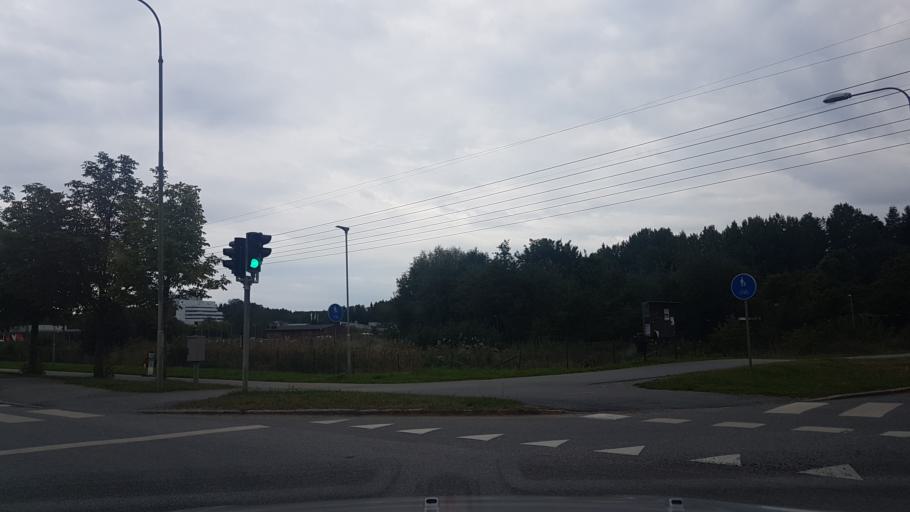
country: SE
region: Stockholm
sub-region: Jarfalla Kommun
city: Jakobsberg
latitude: 59.4164
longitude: 17.8236
